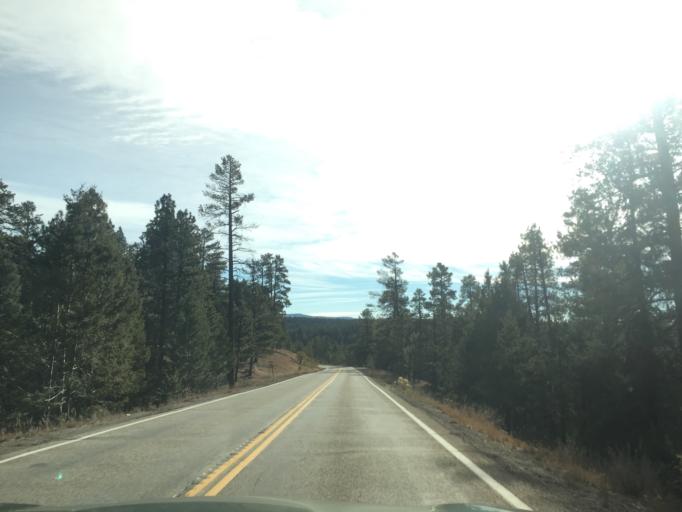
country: US
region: Utah
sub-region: Garfield County
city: Panguitch
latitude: 37.4921
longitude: -112.6178
